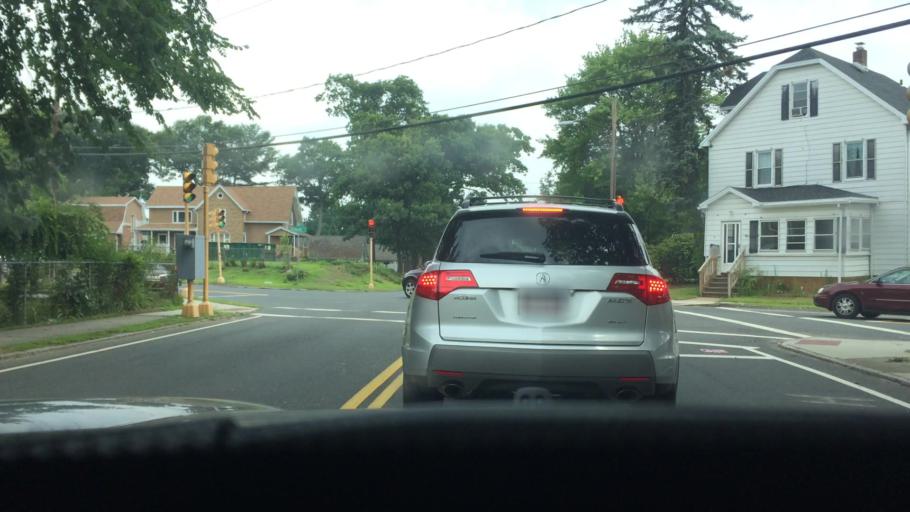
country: US
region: Massachusetts
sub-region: Hampden County
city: Springfield
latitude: 42.1297
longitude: -72.5846
